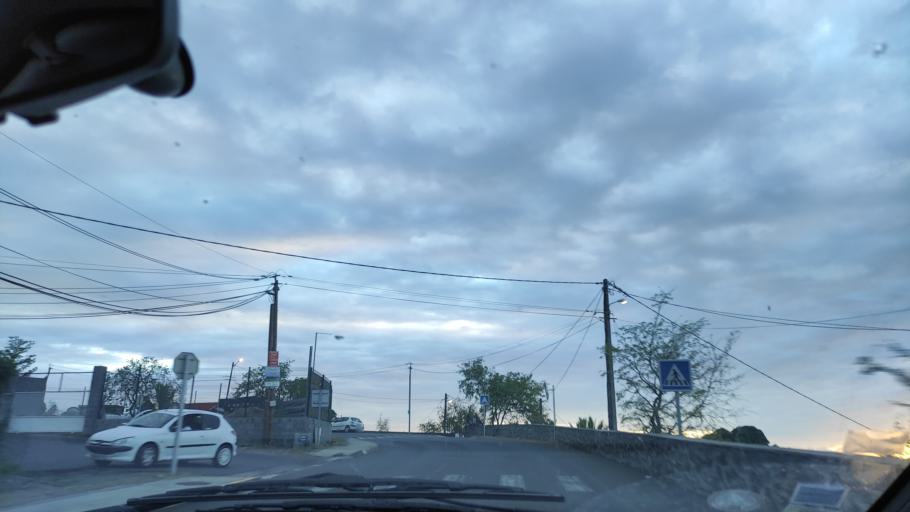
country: RE
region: Reunion
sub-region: Reunion
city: Saint-Leu
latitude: -21.1962
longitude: 55.2922
